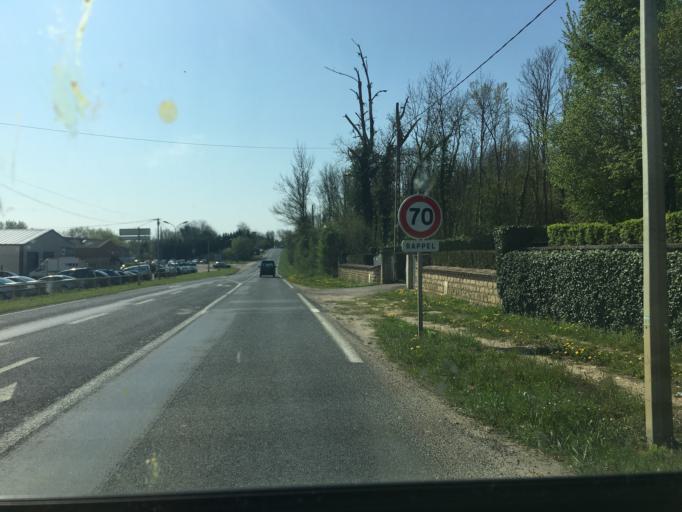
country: FR
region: Lorraine
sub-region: Departement de Meurthe-et-Moselle
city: Norroy-les-Pont-a-Mousson
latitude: 48.9306
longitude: 6.0376
